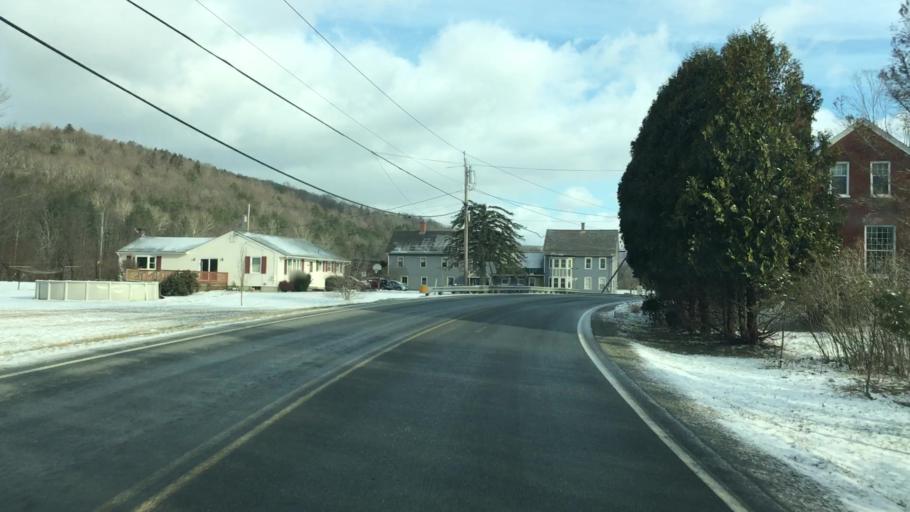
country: US
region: Massachusetts
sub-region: Franklin County
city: Colrain
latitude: 42.7082
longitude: -72.7029
